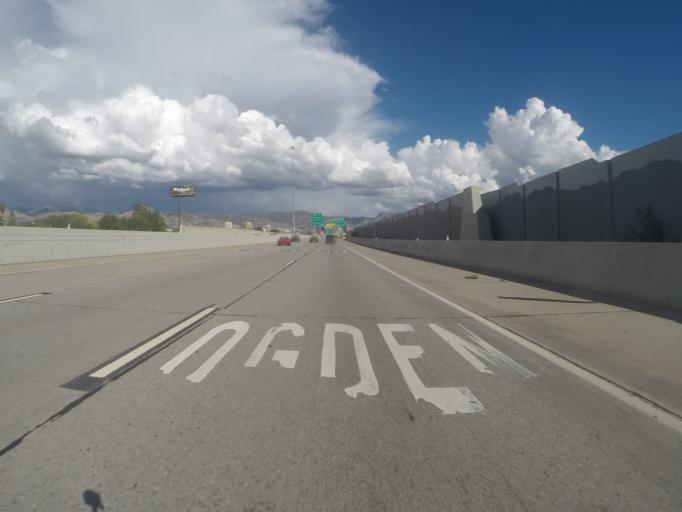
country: US
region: Utah
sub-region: Salt Lake County
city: Salt Lake City
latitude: 40.7645
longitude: -111.9240
